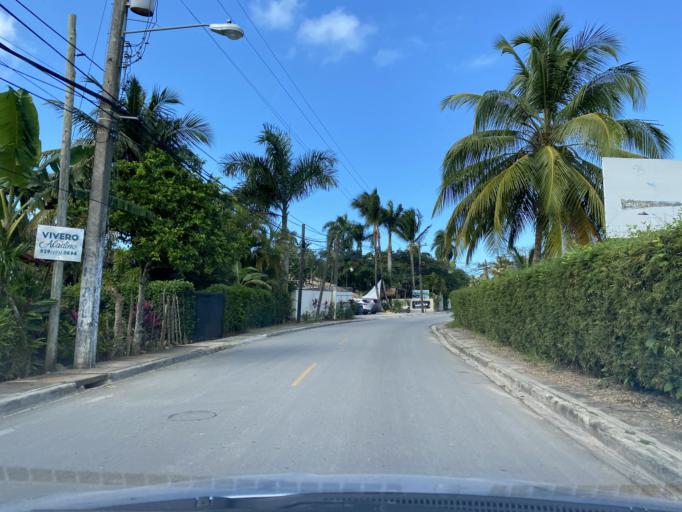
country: DO
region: Samana
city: Las Terrenas
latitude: 19.3084
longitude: -69.5637
